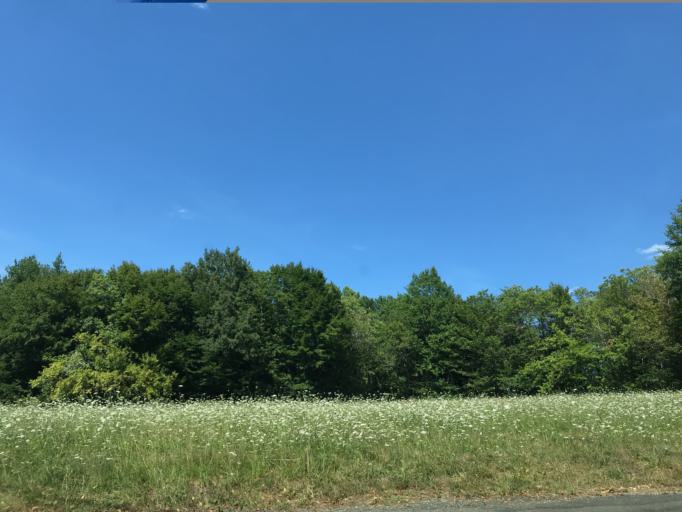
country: FR
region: Aquitaine
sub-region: Departement de la Dordogne
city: Sarlat-la-Caneda
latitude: 44.9123
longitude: 1.1686
